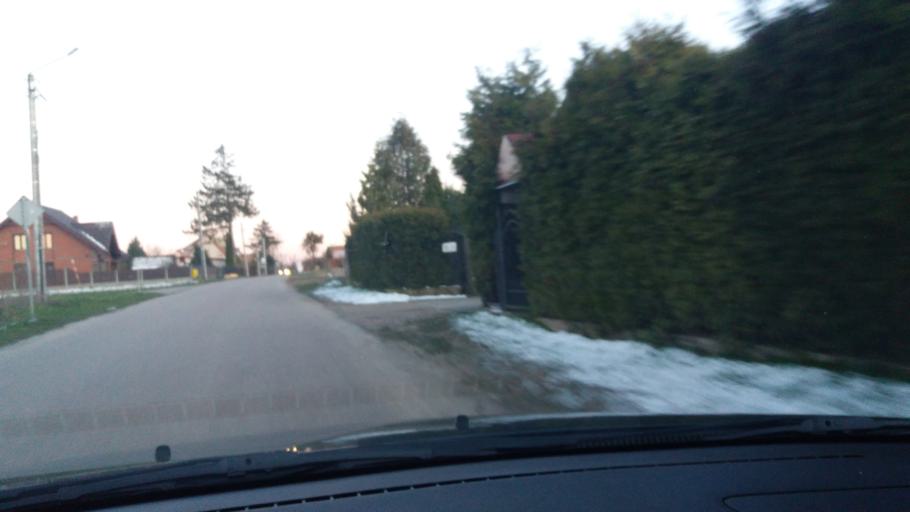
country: PL
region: Warmian-Masurian Voivodeship
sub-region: Powiat szczycienski
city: Szczytno
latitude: 53.5612
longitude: 20.9669
